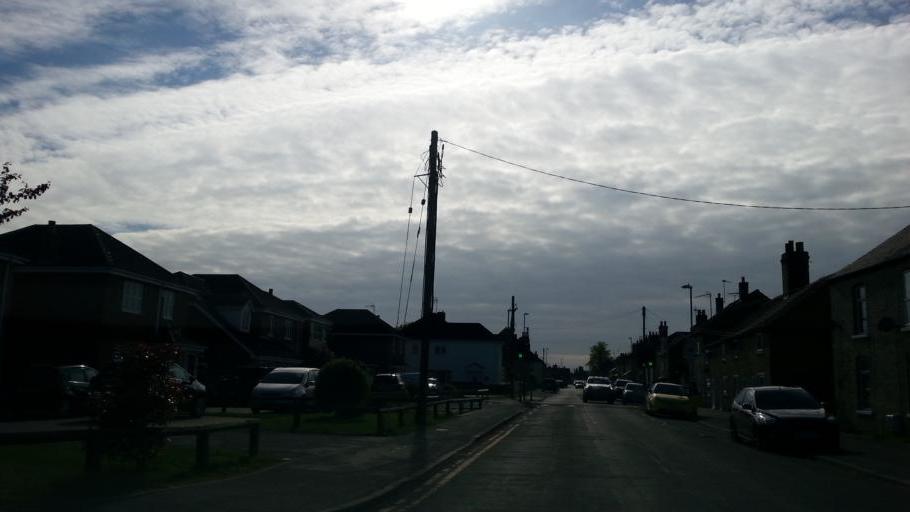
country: GB
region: England
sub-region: Cambridgeshire
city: Chatteris
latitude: 52.4570
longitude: 0.0567
